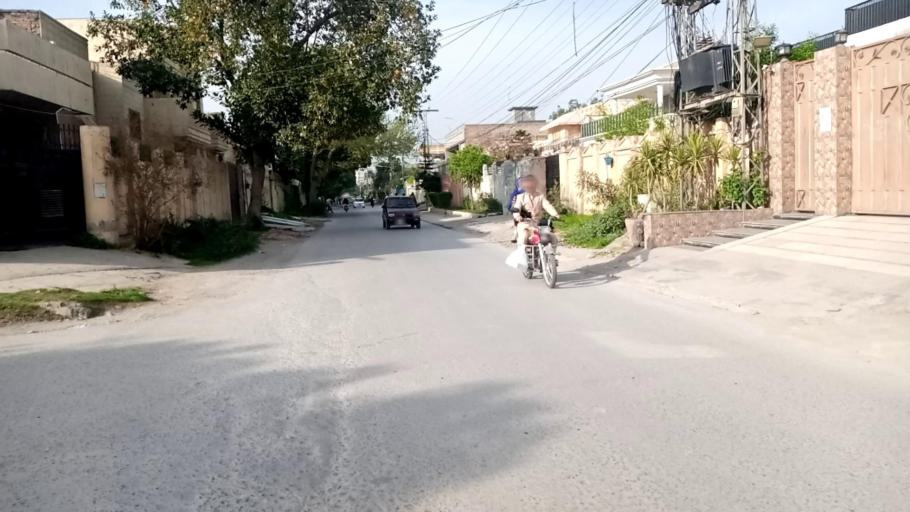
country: PK
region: Khyber Pakhtunkhwa
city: Peshawar
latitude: 33.9747
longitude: 71.4381
